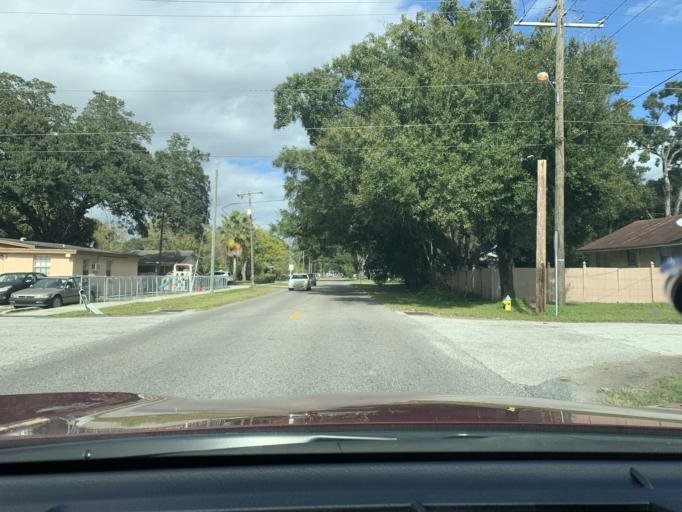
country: US
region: Florida
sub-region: Hillsborough County
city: Tampa
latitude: 27.9695
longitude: -82.4931
